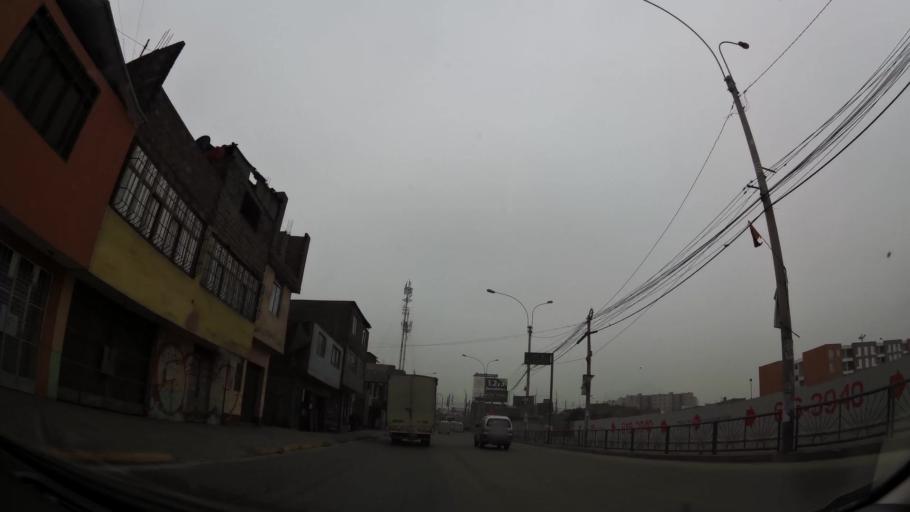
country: PE
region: Lima
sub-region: Lima
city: Santa Maria
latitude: -12.0170
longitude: -76.8980
